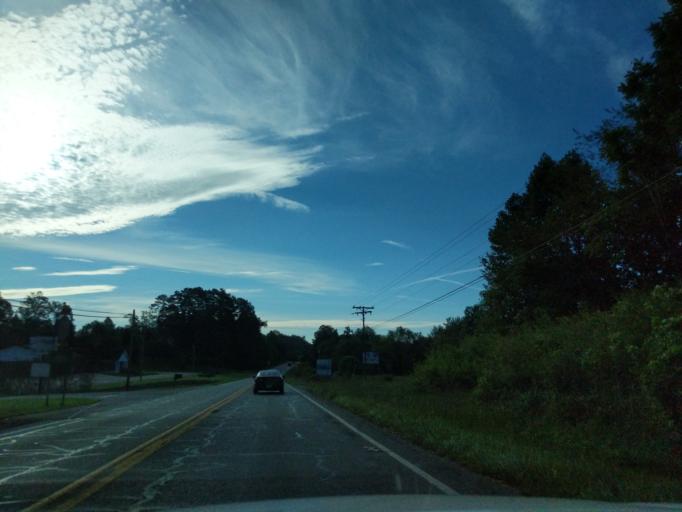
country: US
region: Georgia
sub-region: Fannin County
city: Blue Ridge
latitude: 34.8938
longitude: -84.3539
